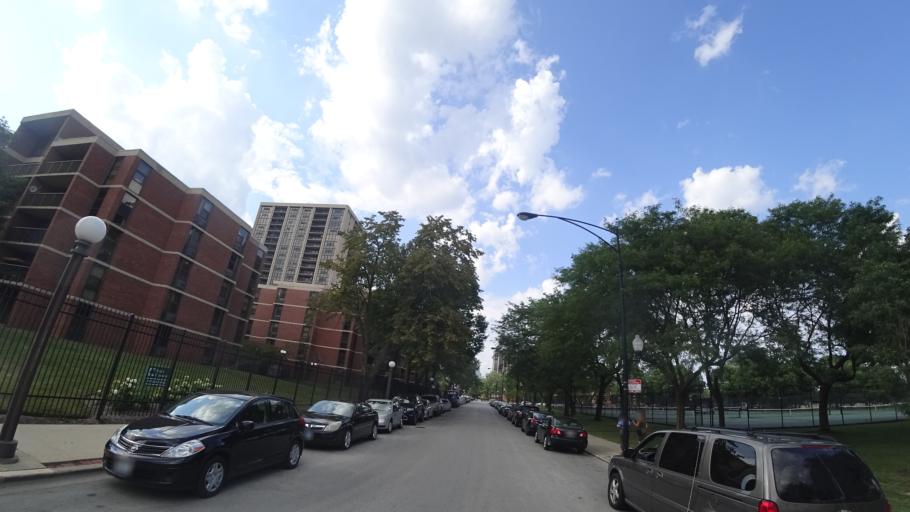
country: US
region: Illinois
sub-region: Cook County
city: Chicago
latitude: 41.8403
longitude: -87.6219
